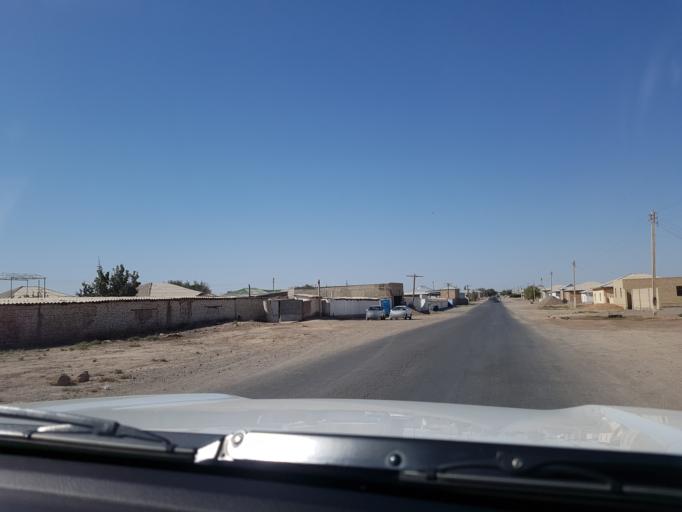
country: IR
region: Razavi Khorasan
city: Sarakhs
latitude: 36.5141
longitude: 61.2223
